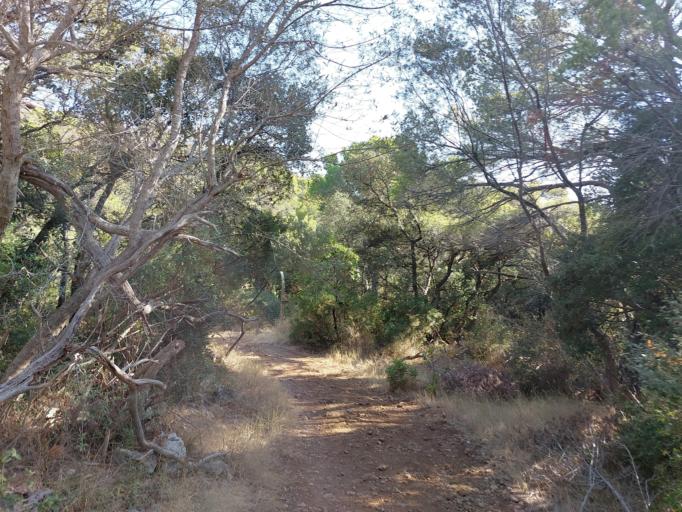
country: HR
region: Dubrovacko-Neretvanska
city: Smokvica
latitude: 42.7587
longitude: 16.8083
